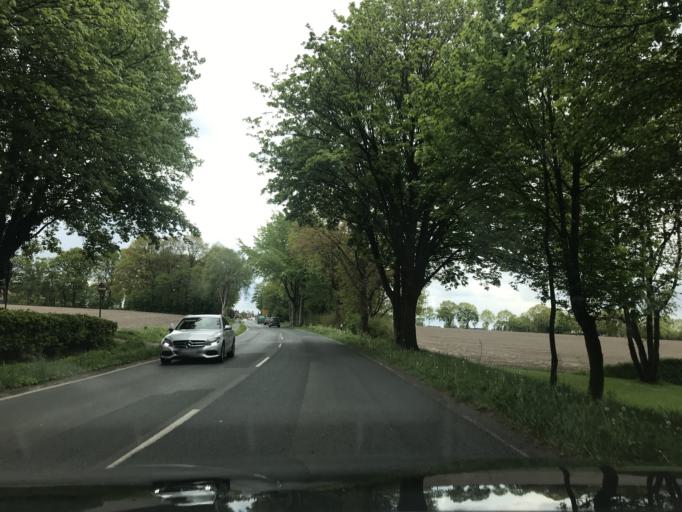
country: DE
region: Lower Saxony
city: Ganderkesee
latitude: 53.0494
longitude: 8.5353
